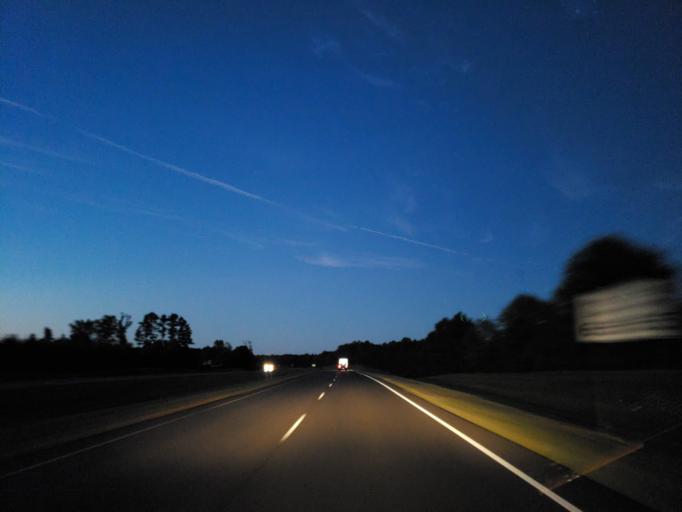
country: US
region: Mississippi
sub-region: Clarke County
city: Quitman
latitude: 32.0423
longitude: -88.6777
